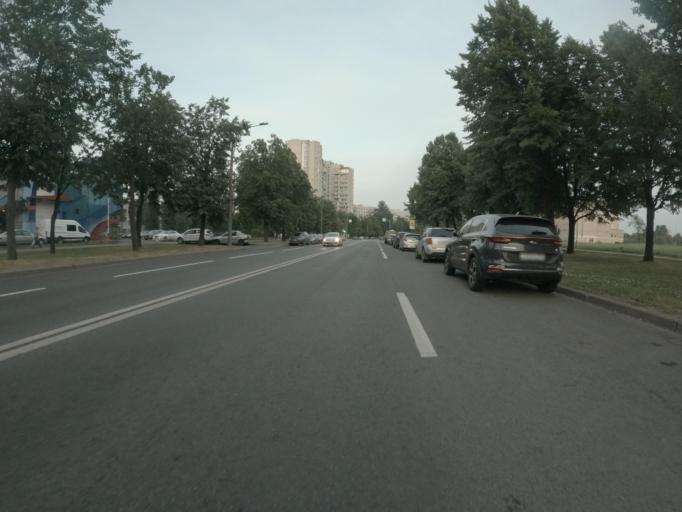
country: RU
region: St.-Petersburg
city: Krasnogvargeisky
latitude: 59.9675
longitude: 30.4286
